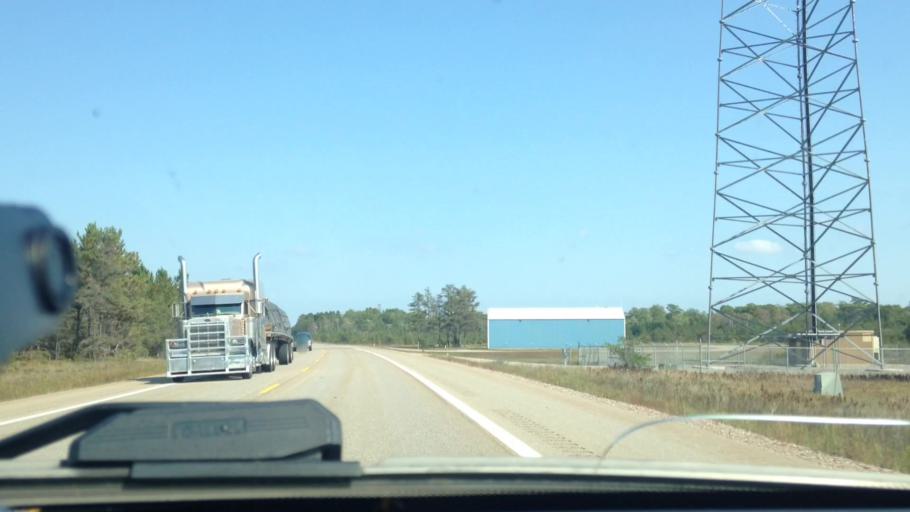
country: US
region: Michigan
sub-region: Chippewa County
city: Sault Ste. Marie
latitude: 46.3591
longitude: -84.7920
